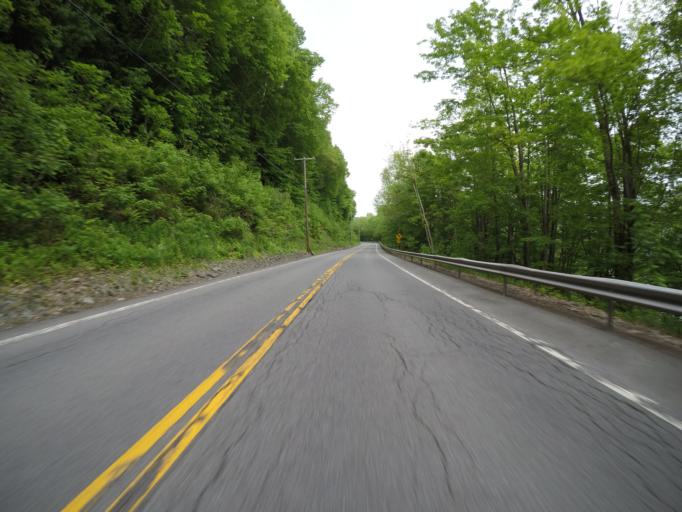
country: US
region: New York
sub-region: Delaware County
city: Delhi
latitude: 42.0780
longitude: -74.9302
